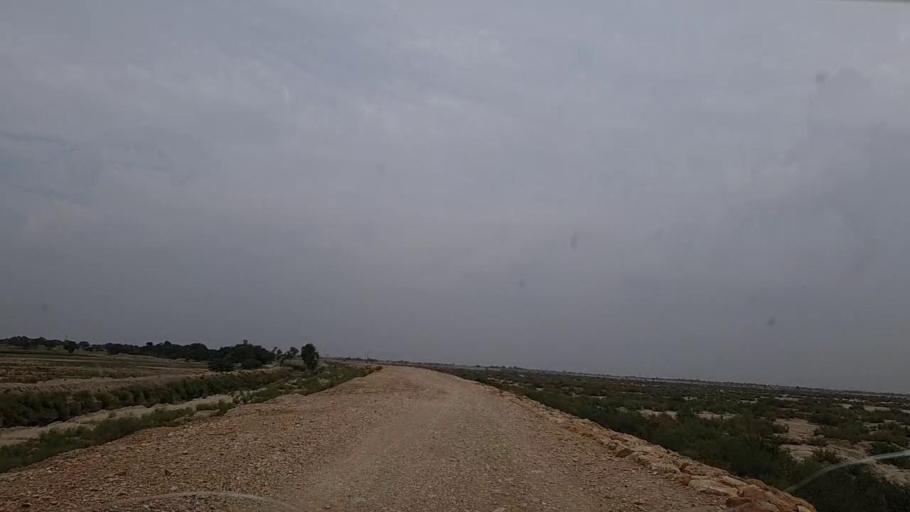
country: PK
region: Sindh
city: Johi
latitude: 26.7083
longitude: 67.5874
